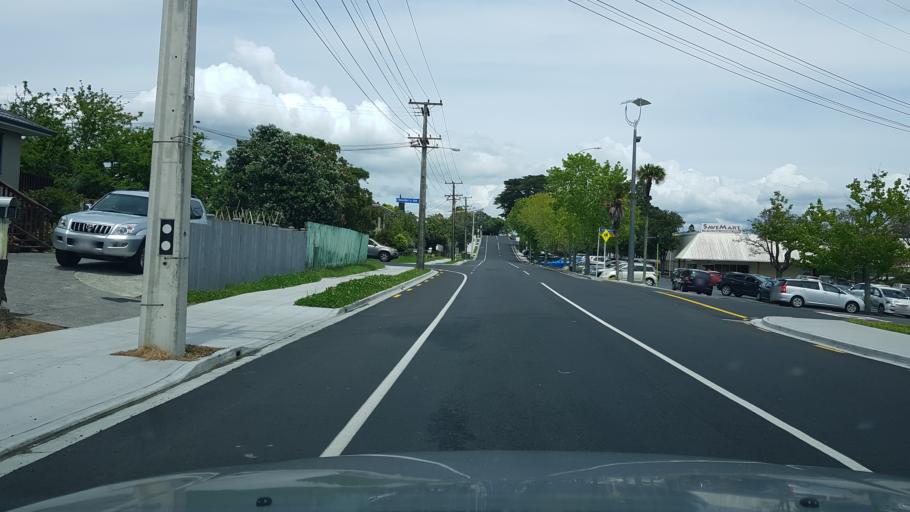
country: NZ
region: Auckland
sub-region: Auckland
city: North Shore
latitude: -36.8013
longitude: 174.7477
